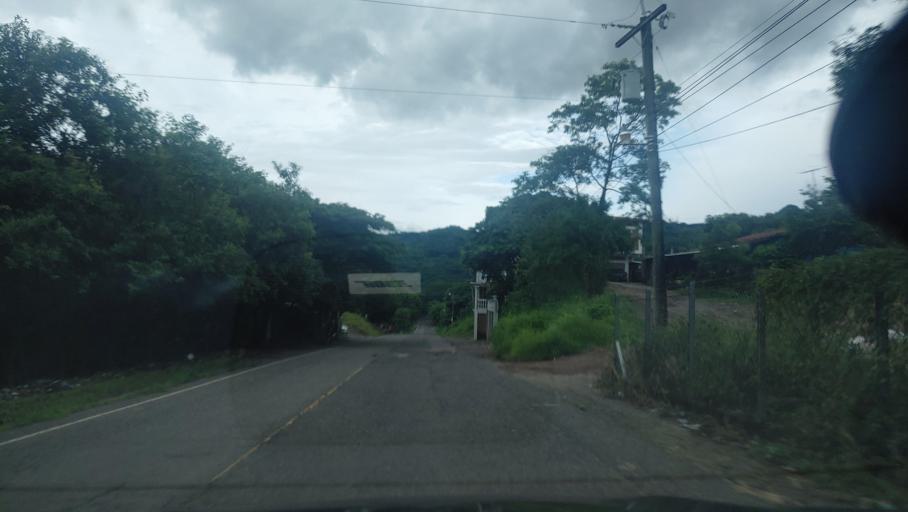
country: HN
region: Choluteca
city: Corpus
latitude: 13.3697
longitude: -87.0320
